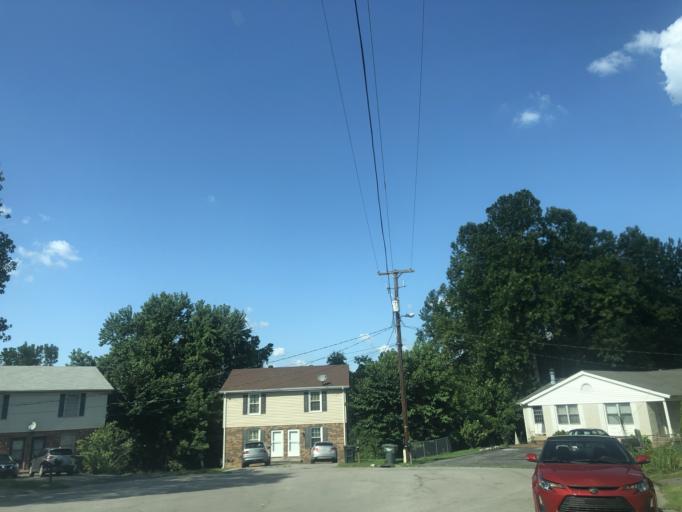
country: US
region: Tennessee
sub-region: Wilson County
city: Green Hill
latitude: 36.2133
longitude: -86.5921
